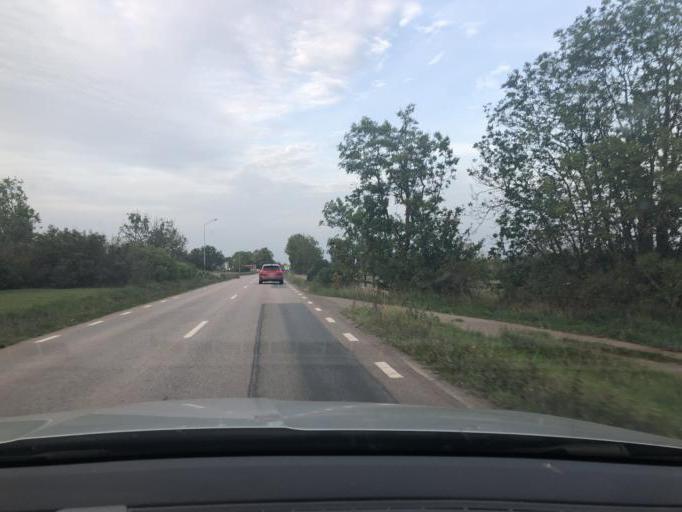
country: SE
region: Kalmar
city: Faerjestaden
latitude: 56.6092
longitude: 16.4787
